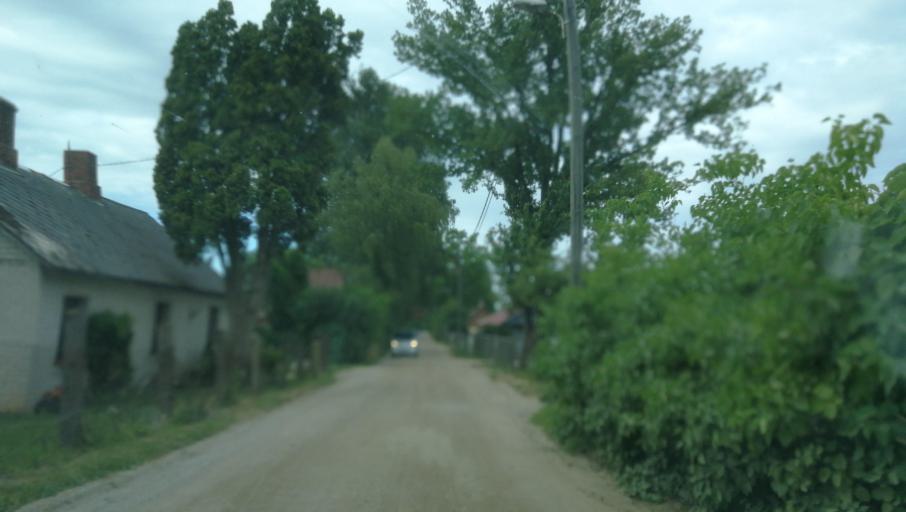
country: LV
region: Cesu Rajons
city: Cesis
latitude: 57.3109
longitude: 25.2938
